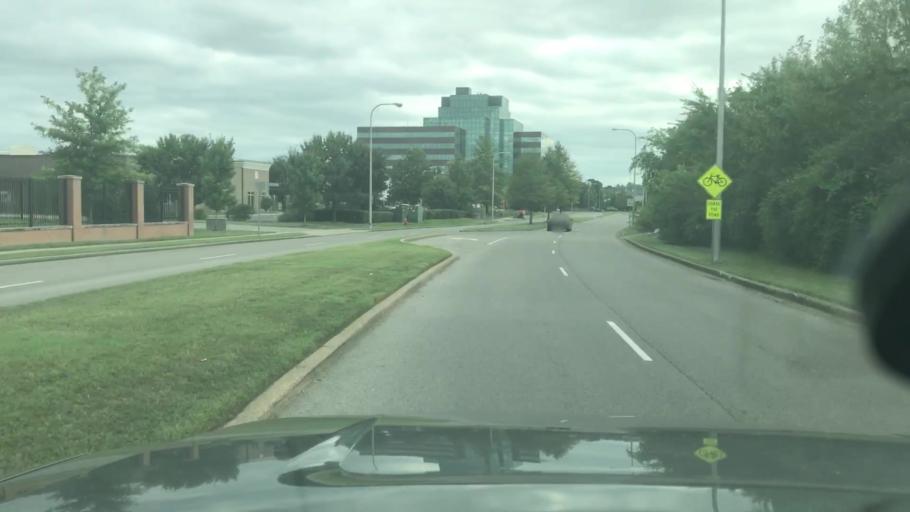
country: US
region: Tennessee
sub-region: Davidson County
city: Nashville
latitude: 36.1988
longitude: -86.7984
